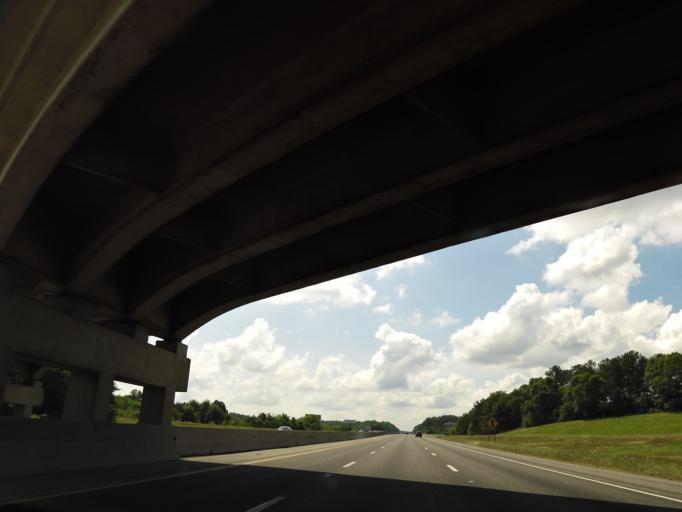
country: US
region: Alabama
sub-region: Saint Clair County
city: Riverside
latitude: 33.5986
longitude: -86.2125
